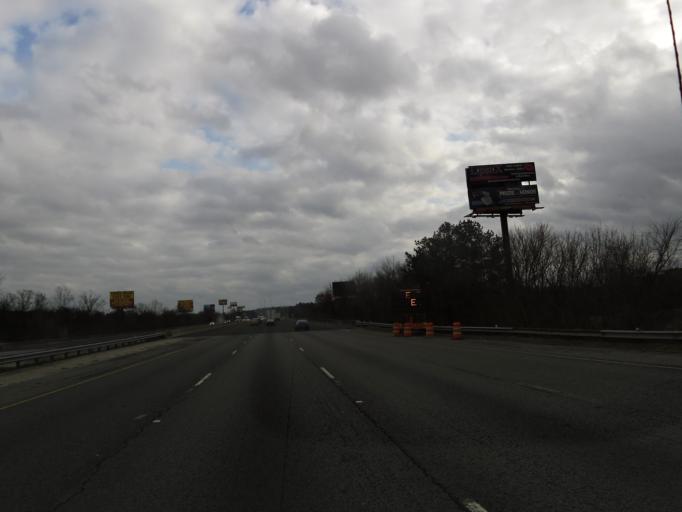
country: US
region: Georgia
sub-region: Gordon County
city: Calhoun
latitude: 34.5734
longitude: -84.9482
